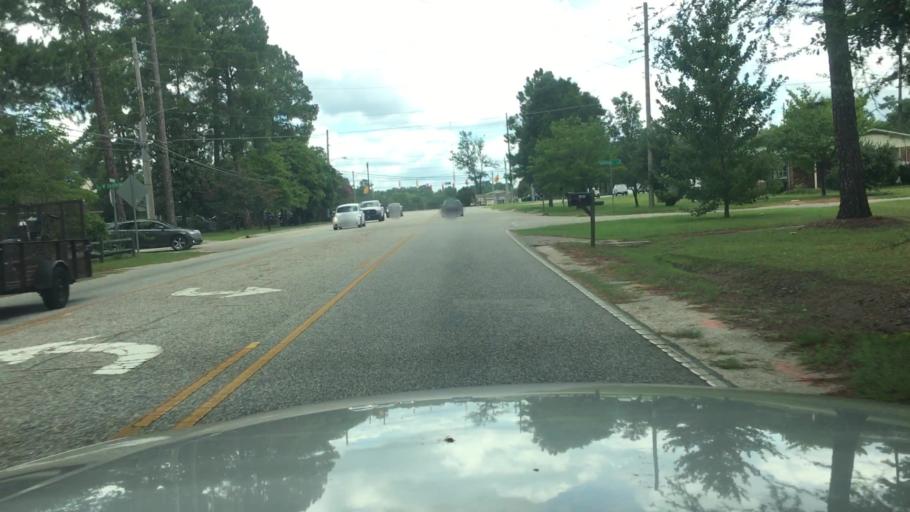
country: US
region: North Carolina
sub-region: Cumberland County
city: Hope Mills
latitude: 35.0417
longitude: -78.9854
